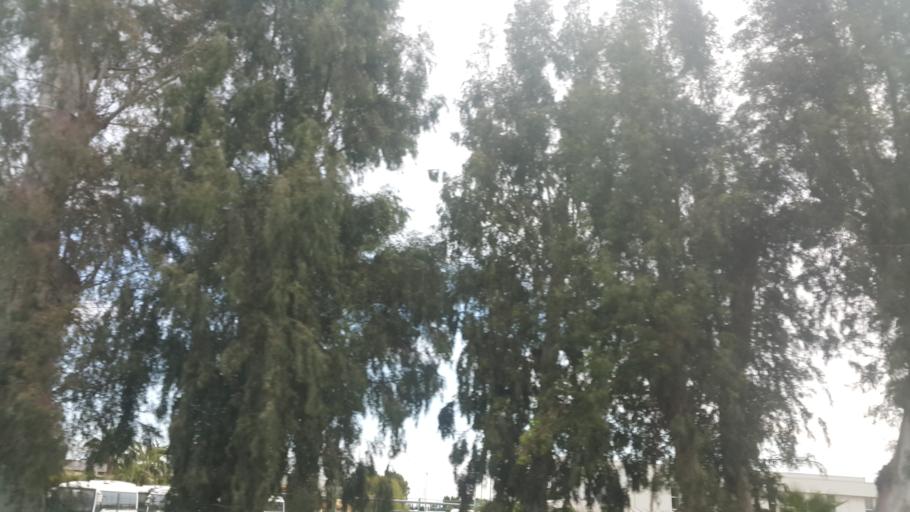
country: TR
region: Adana
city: Seyhan
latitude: 36.9927
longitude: 35.1884
